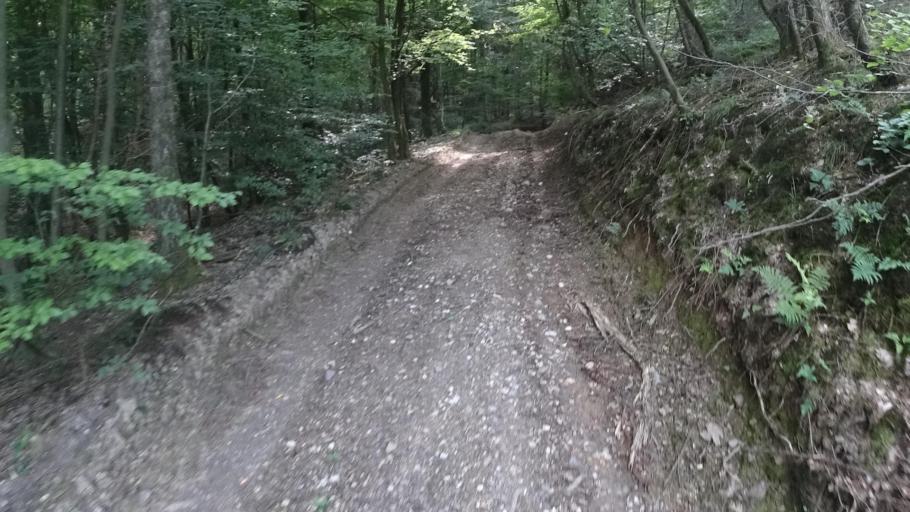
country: DE
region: Rheinland-Pfalz
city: Sankt Katharinen
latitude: 50.5756
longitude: 7.3575
